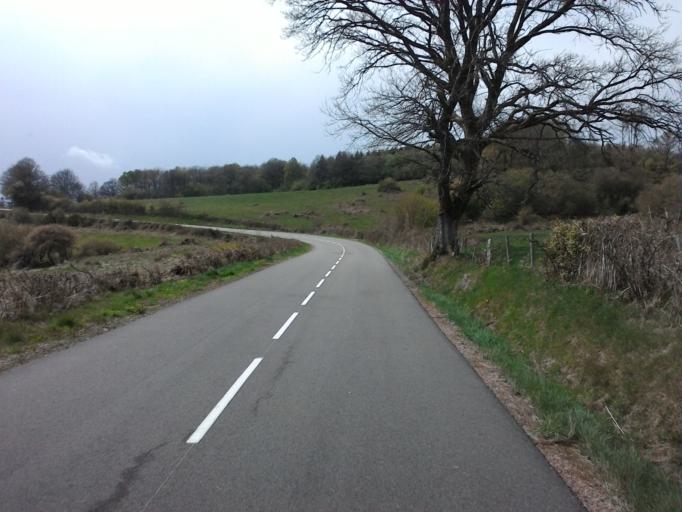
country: FR
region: Bourgogne
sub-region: Departement de la Cote-d'Or
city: Saulieu
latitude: 47.1811
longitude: 4.0928
